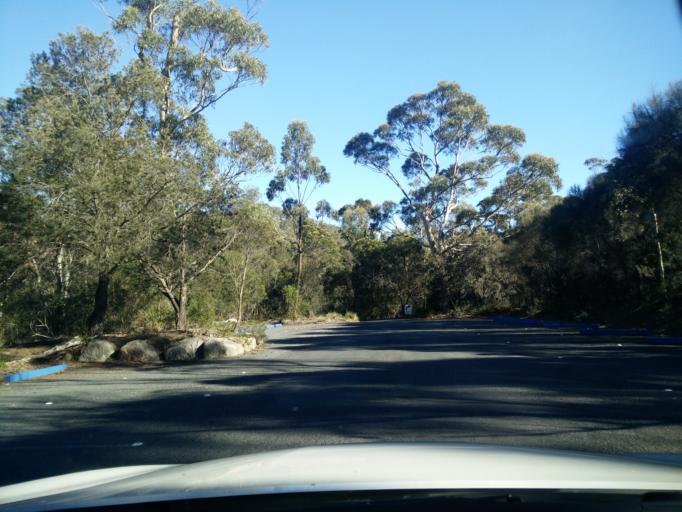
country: AU
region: Tasmania
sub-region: Break O'Day
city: St Helens
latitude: -42.1242
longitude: 148.2978
